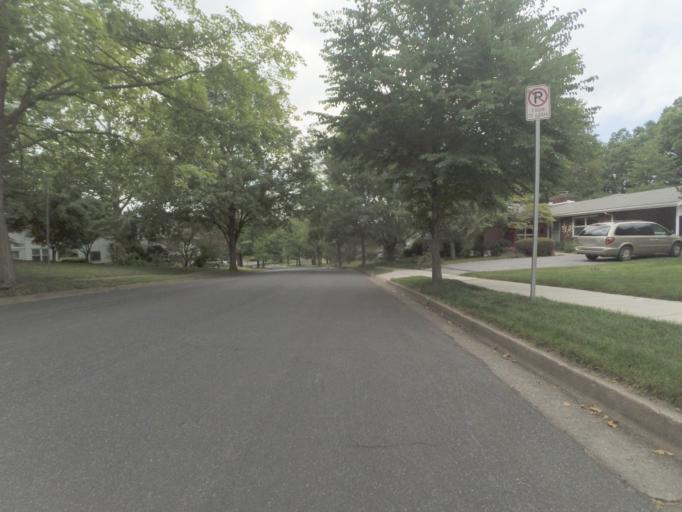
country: US
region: Pennsylvania
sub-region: Centre County
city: State College
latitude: 40.7907
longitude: -77.8451
